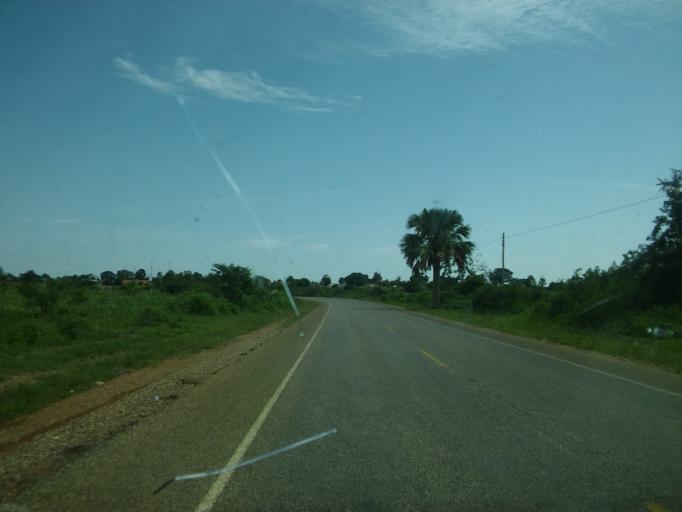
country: UG
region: Eastern Region
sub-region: Bukedea District
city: Bukedea
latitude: 1.3360
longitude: 34.0545
